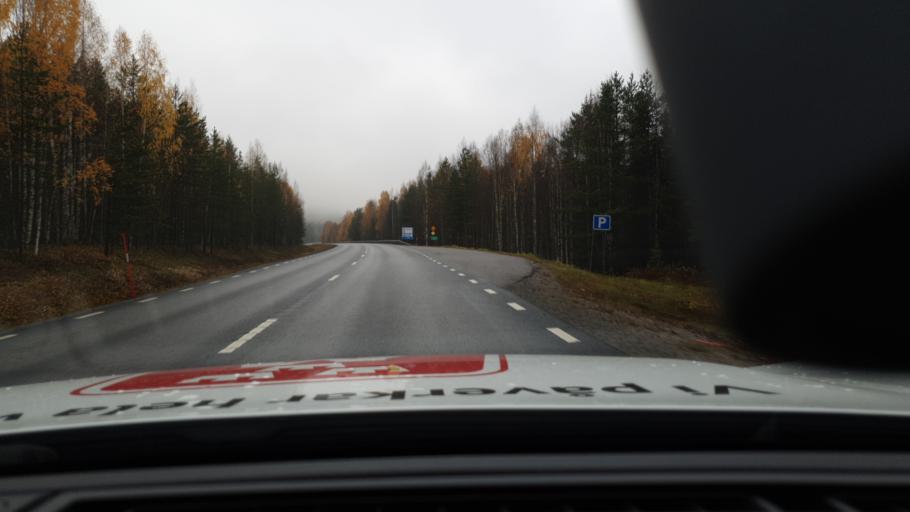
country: SE
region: Norrbotten
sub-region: Overkalix Kommun
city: OEverkalix
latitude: 66.6420
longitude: 22.1965
